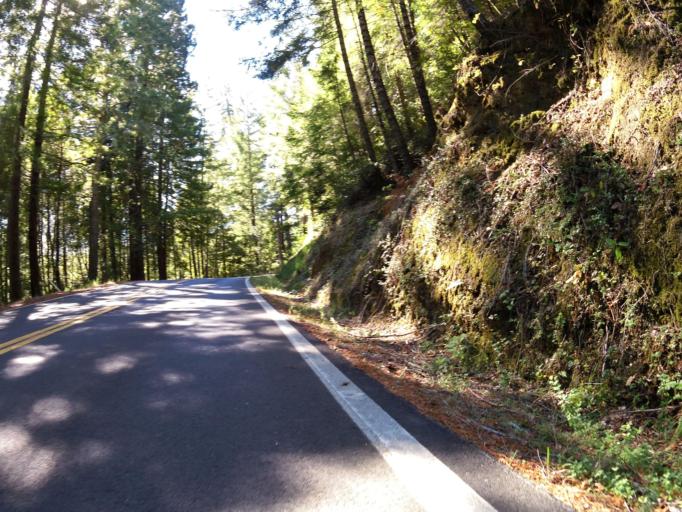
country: US
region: California
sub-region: Humboldt County
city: Redway
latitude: 39.8540
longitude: -123.7295
